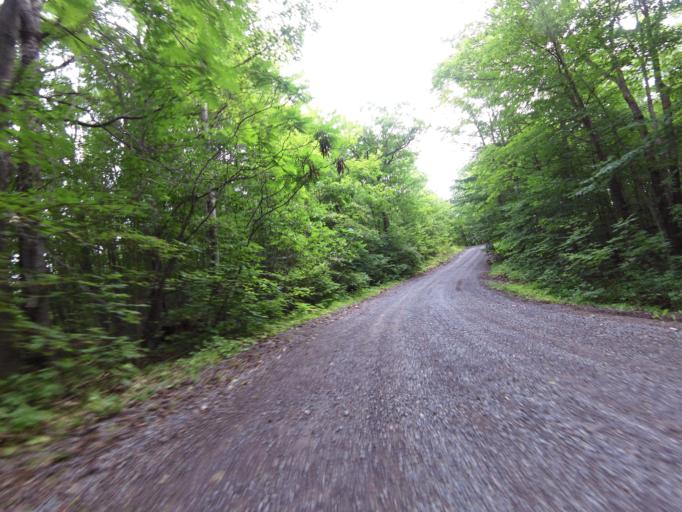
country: CA
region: Ontario
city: Kingston
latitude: 44.5629
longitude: -76.5740
